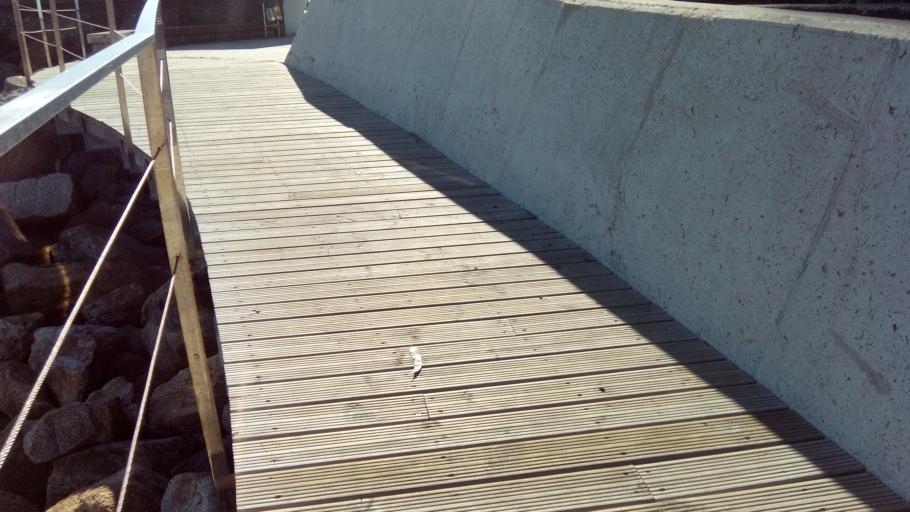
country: ES
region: Galicia
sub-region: Provincia de Pontevedra
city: Baiona
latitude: 42.1252
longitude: -8.8468
